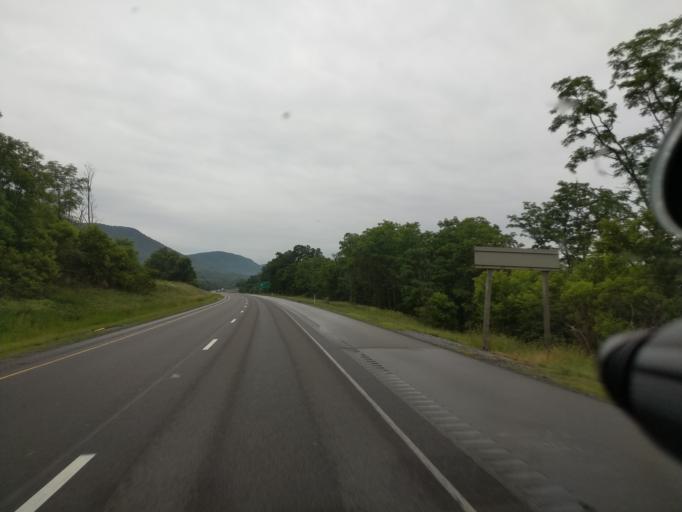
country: US
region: Pennsylvania
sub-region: Clinton County
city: Castanea
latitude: 41.0618
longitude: -77.4298
